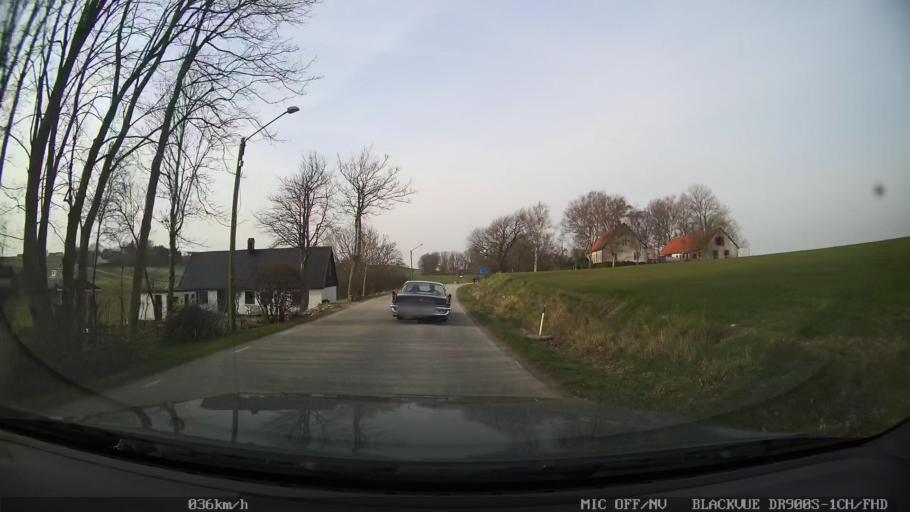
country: SE
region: Skane
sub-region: Ystads Kommun
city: Ystad
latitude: 55.4640
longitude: 13.8226
